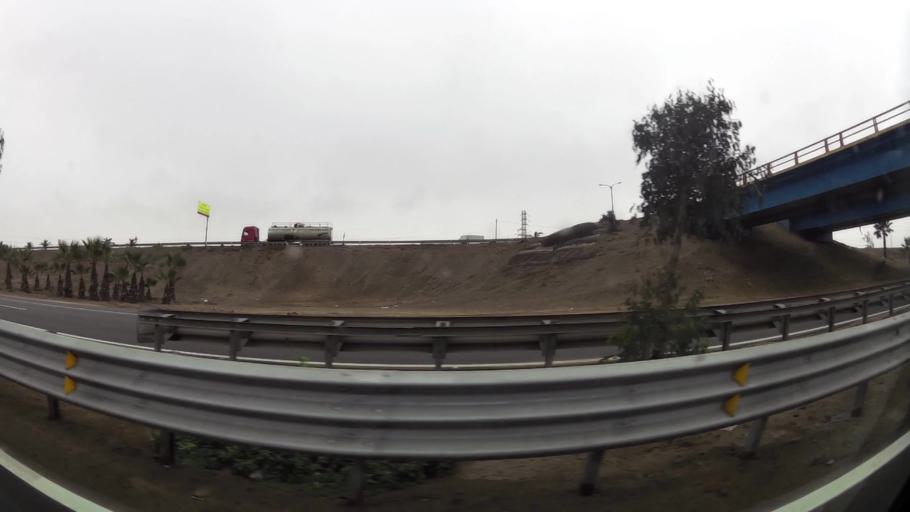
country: PE
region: Lima
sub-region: Lima
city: Punta Hermosa
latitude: -12.3019
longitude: -76.8449
